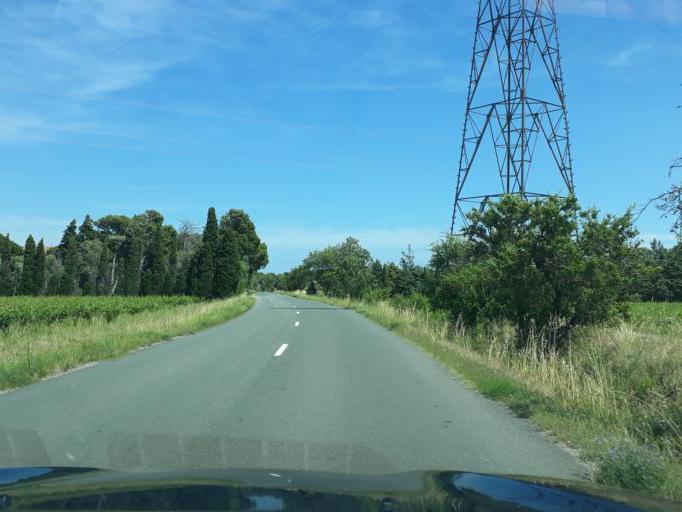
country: FR
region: Languedoc-Roussillon
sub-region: Departement de l'Aude
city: Portel-des-Corbieres
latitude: 43.0399
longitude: 2.9415
